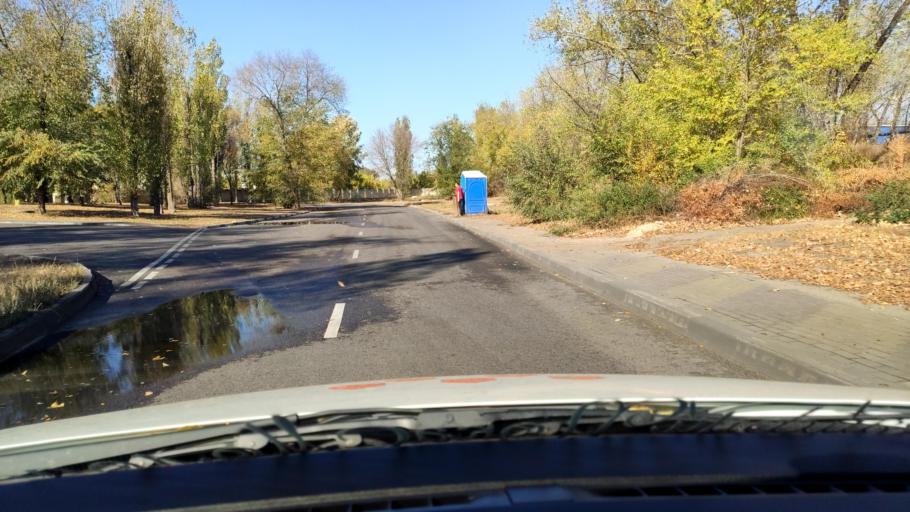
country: RU
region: Voronezj
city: Pridonskoy
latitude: 51.6861
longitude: 39.0625
